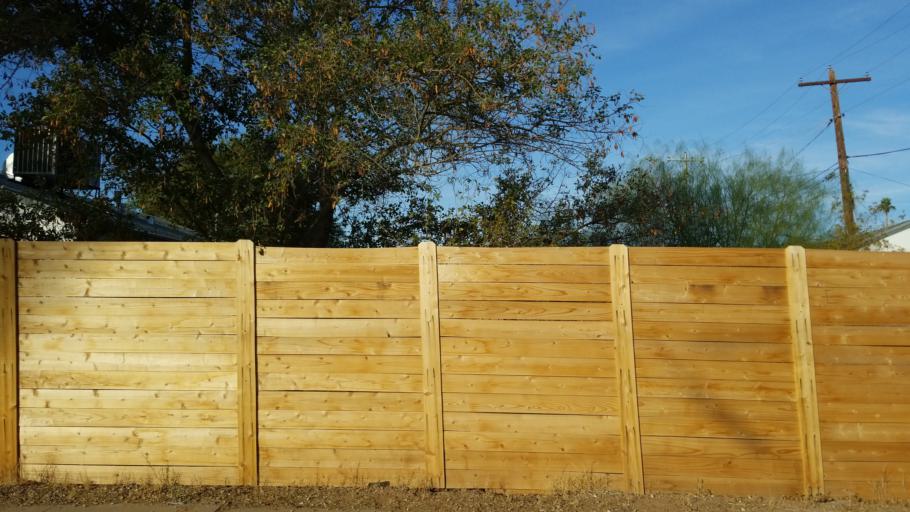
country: US
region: Arizona
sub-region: Maricopa County
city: Phoenix
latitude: 33.4917
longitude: -112.0870
